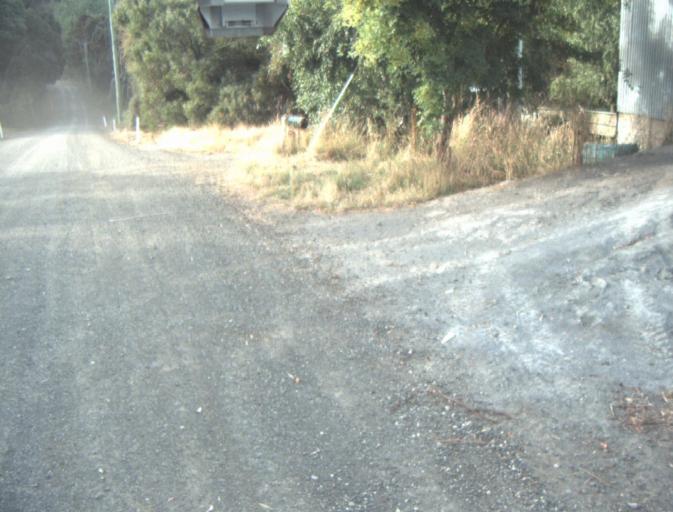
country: AU
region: Tasmania
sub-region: Launceston
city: Mayfield
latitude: -41.2731
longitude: 147.1835
